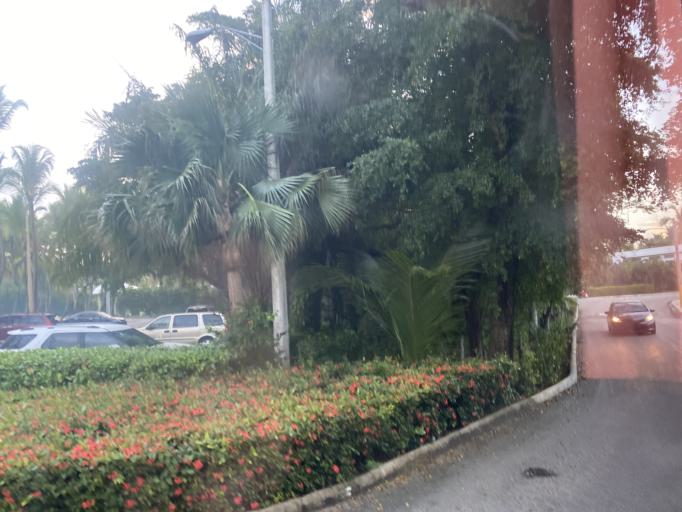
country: DO
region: San Juan
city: Punta Cana
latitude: 18.7190
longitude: -68.4567
